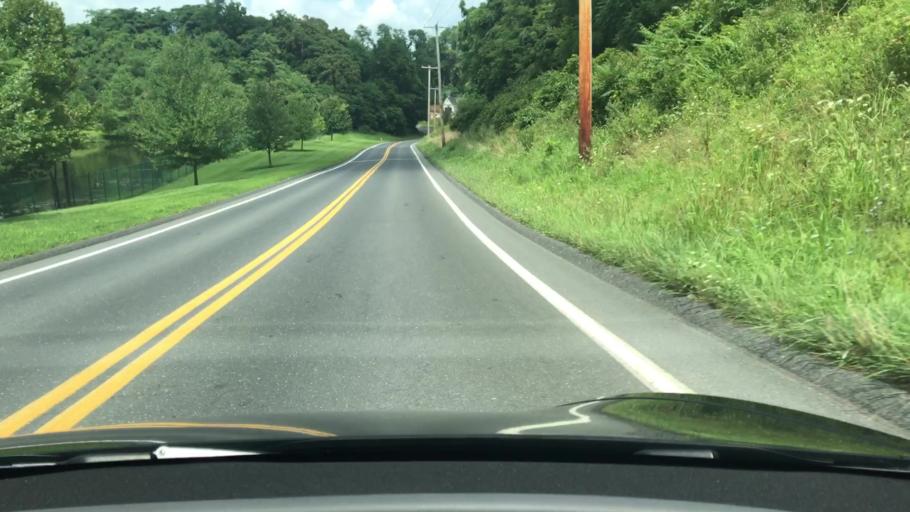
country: US
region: Pennsylvania
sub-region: Cumberland County
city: New Cumberland
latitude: 40.1984
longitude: -76.8782
